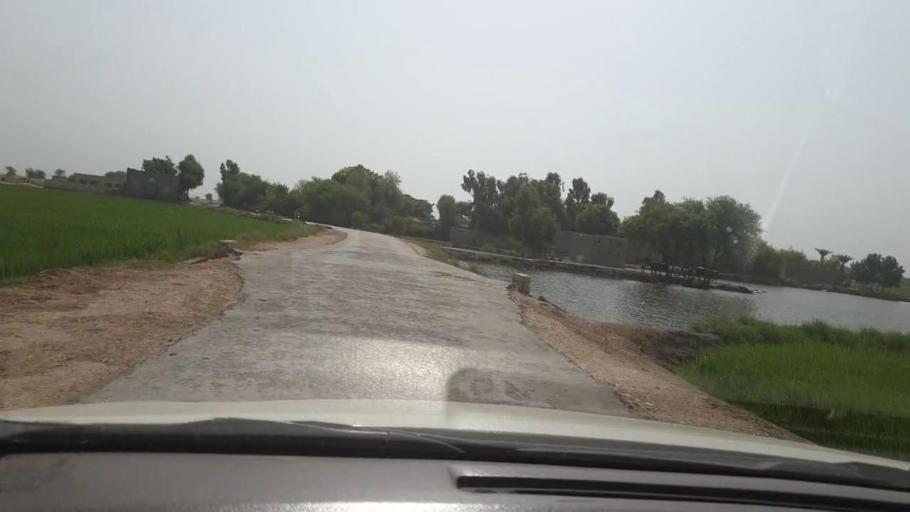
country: PK
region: Sindh
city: Rustam jo Goth
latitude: 27.9770
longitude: 68.7949
